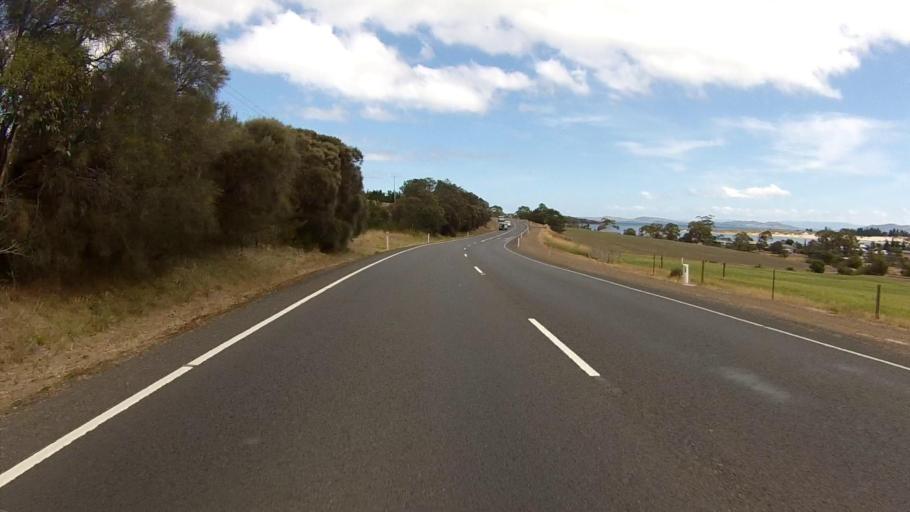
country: AU
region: Tasmania
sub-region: Sorell
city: Sorell
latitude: -42.8360
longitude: 147.6239
